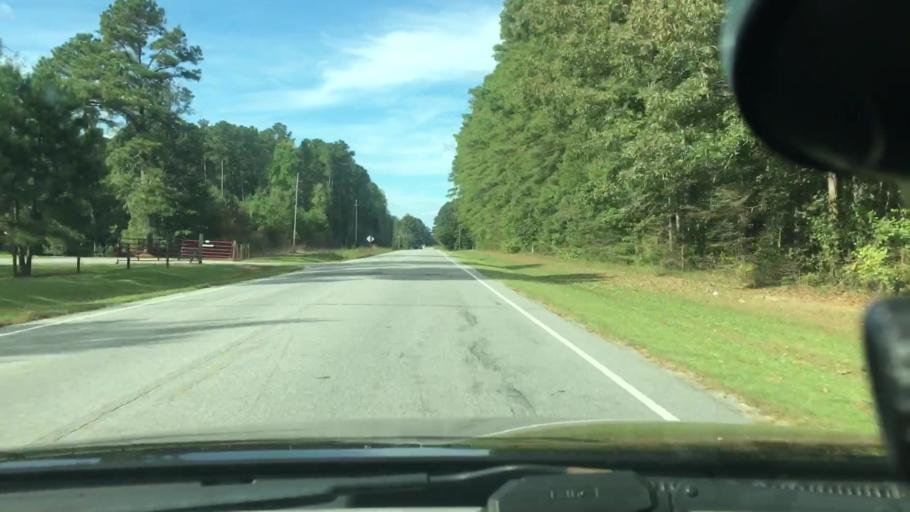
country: US
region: North Carolina
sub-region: Pitt County
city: Windsor
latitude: 35.4402
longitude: -77.2632
